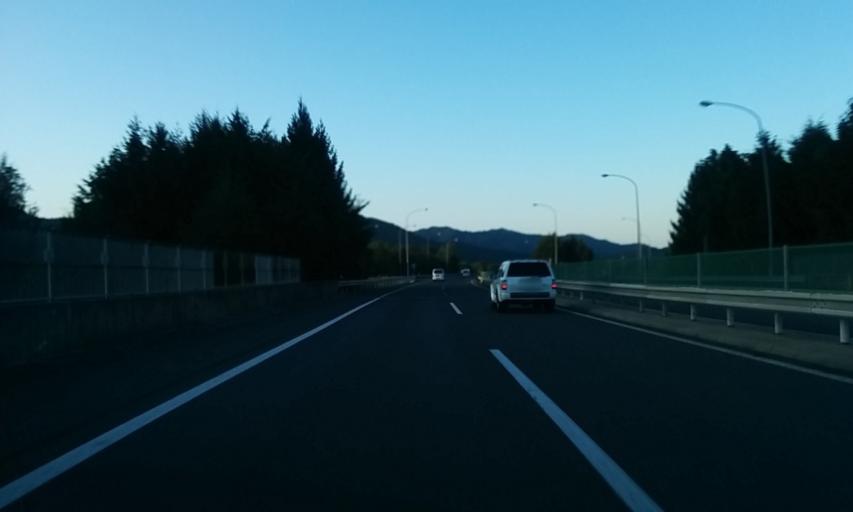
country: JP
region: Kyoto
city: Fukuchiyama
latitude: 35.1641
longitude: 135.1189
